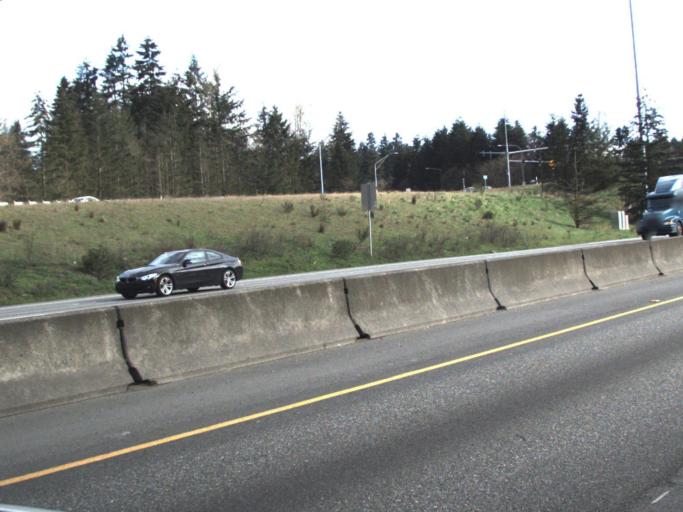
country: US
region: Washington
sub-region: King County
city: Lakeland South
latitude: 47.2936
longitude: -122.2931
